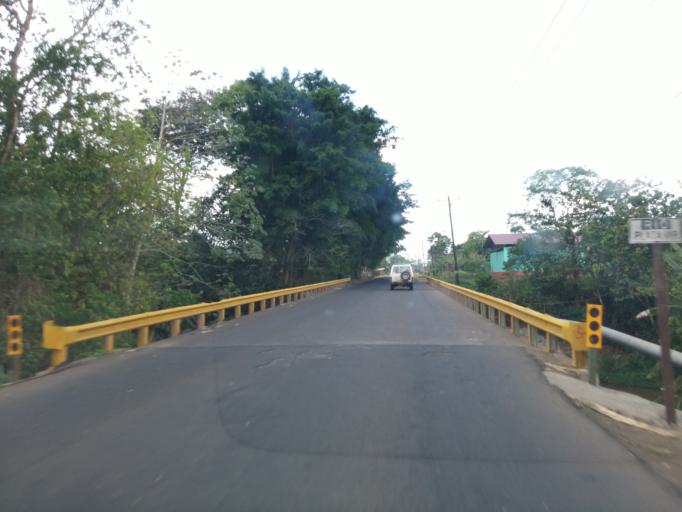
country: CR
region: Alajuela
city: Quesada
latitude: 10.4028
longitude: -84.4731
